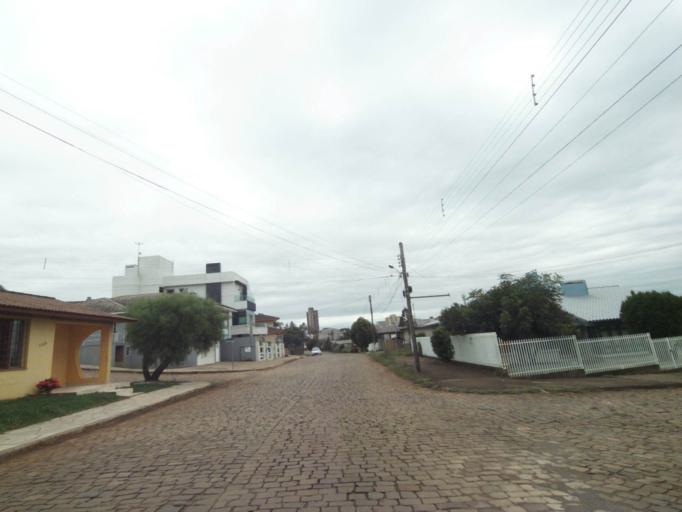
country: BR
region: Rio Grande do Sul
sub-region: Lagoa Vermelha
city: Lagoa Vermelha
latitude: -28.2141
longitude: -51.5305
